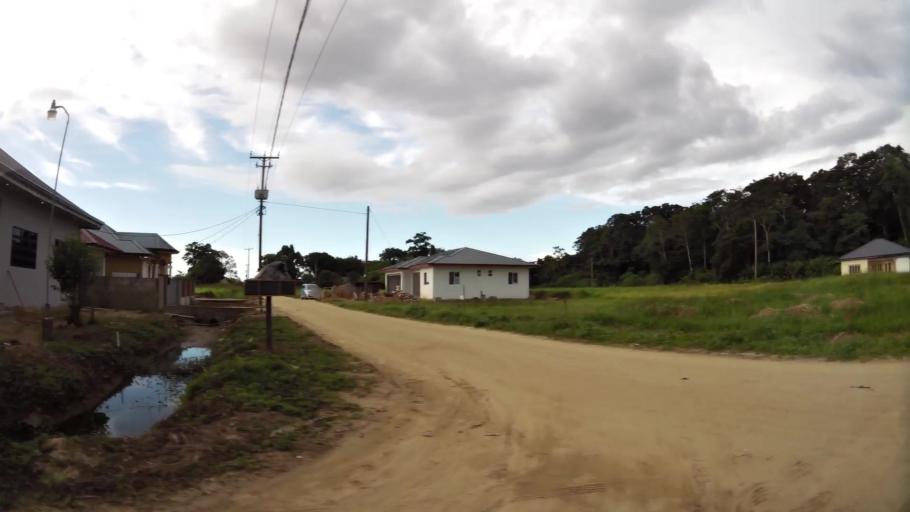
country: SR
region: Paramaribo
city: Paramaribo
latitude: 5.8641
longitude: -55.1798
